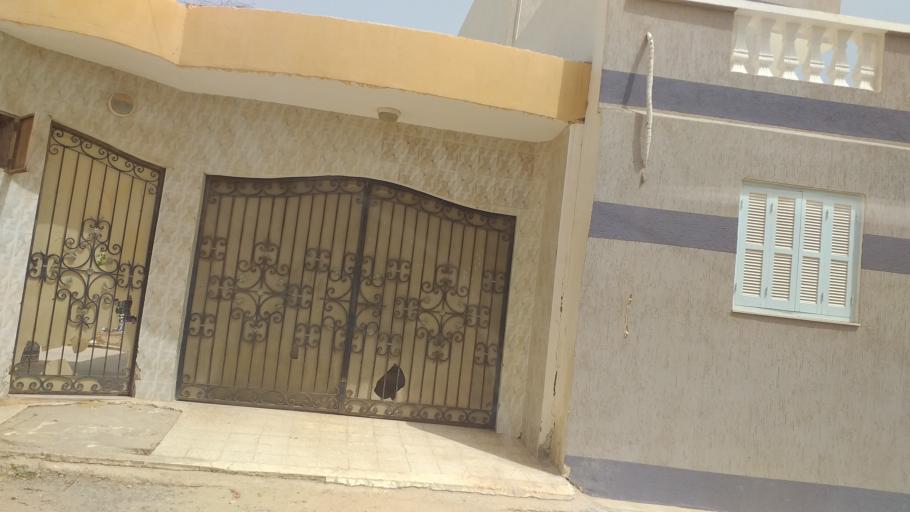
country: TN
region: Qabis
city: Gabes
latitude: 33.9435
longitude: 10.0621
